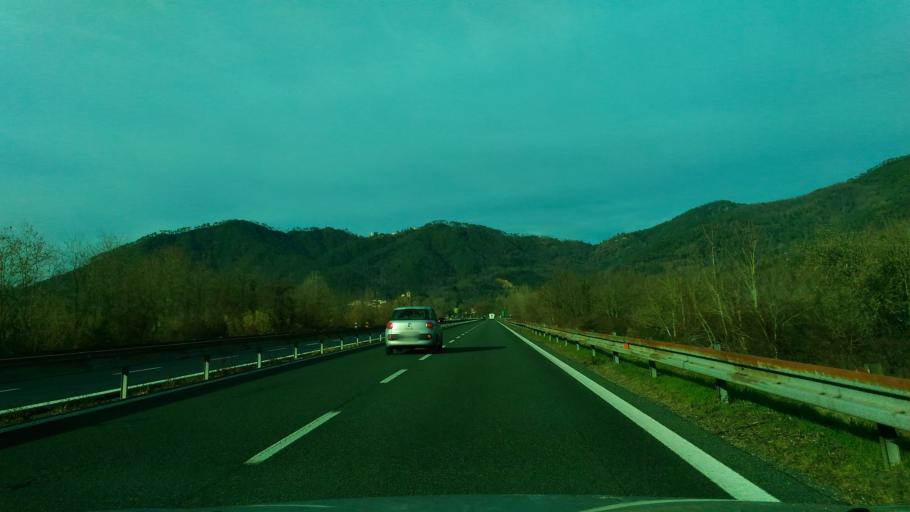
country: IT
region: Liguria
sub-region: Provincia di La Spezia
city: Beverino
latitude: 44.2026
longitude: 9.8035
